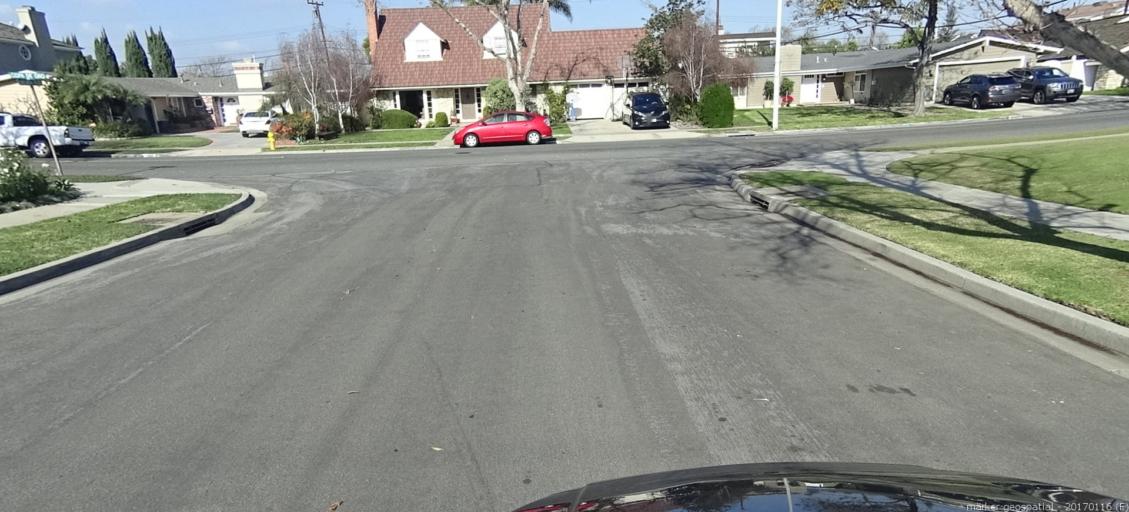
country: US
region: California
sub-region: Orange County
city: Rossmoor
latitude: 33.7810
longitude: -118.0799
